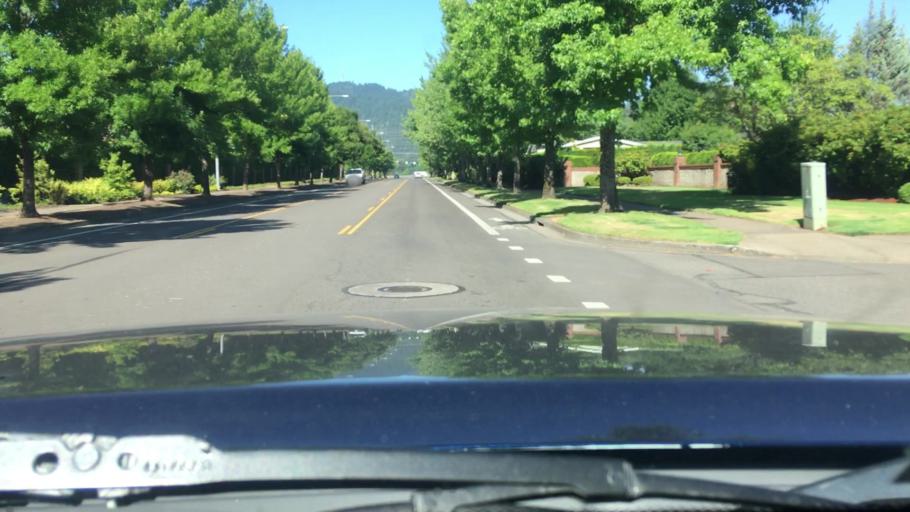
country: US
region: Oregon
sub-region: Lane County
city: Coburg
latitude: 44.0932
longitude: -123.0560
